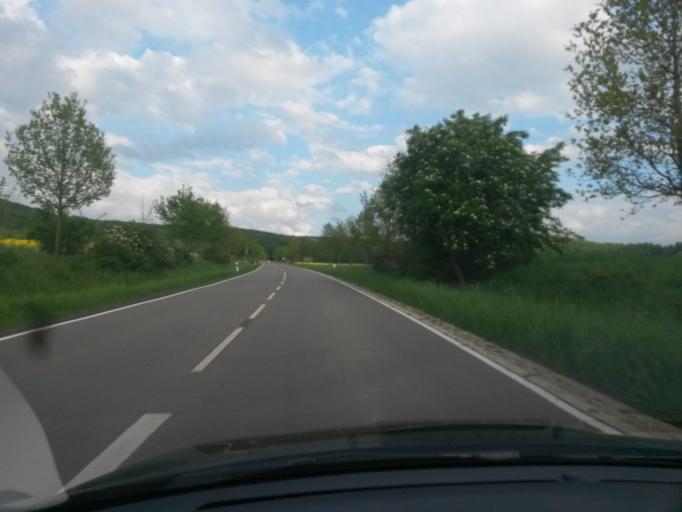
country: DE
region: Hesse
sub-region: Regierungsbezirk Kassel
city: Zierenberg
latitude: 51.3278
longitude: 9.3216
